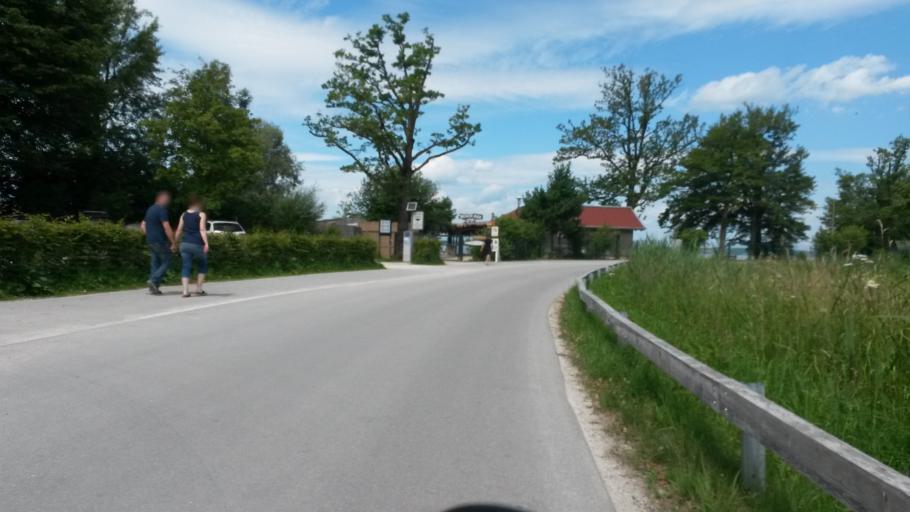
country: DE
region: Bavaria
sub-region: Upper Bavaria
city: Ubersee
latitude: 47.8480
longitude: 12.4756
